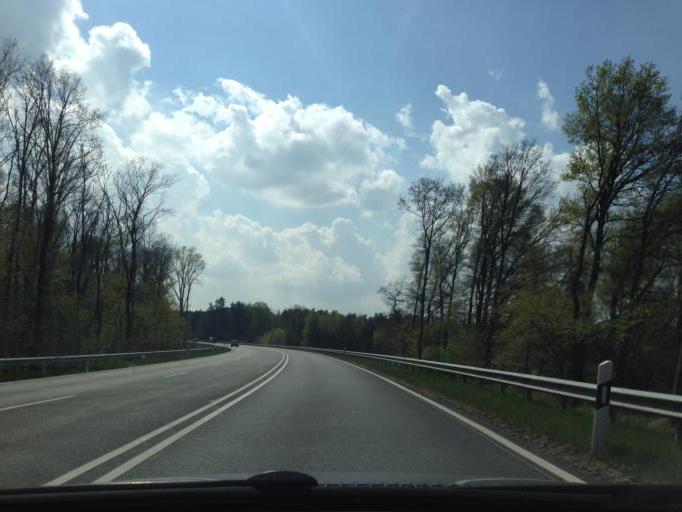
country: DE
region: Lower Saxony
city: Adelheidsdorf
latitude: 52.5909
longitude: 10.0746
